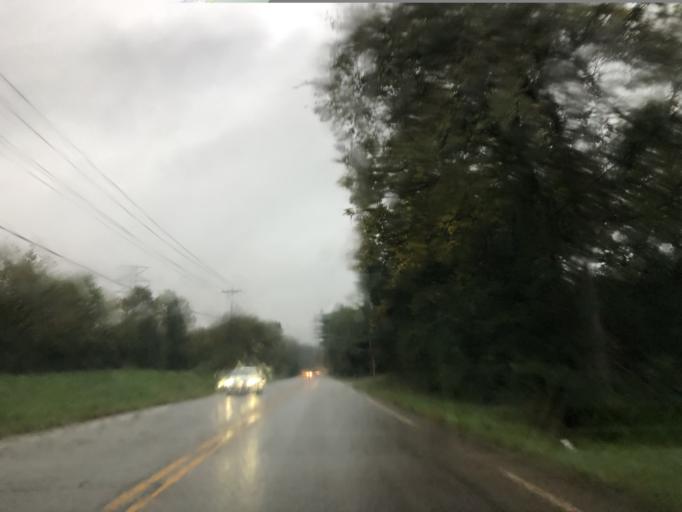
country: US
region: Ohio
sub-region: Hamilton County
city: The Village of Indian Hill
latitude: 39.2295
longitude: -84.3175
